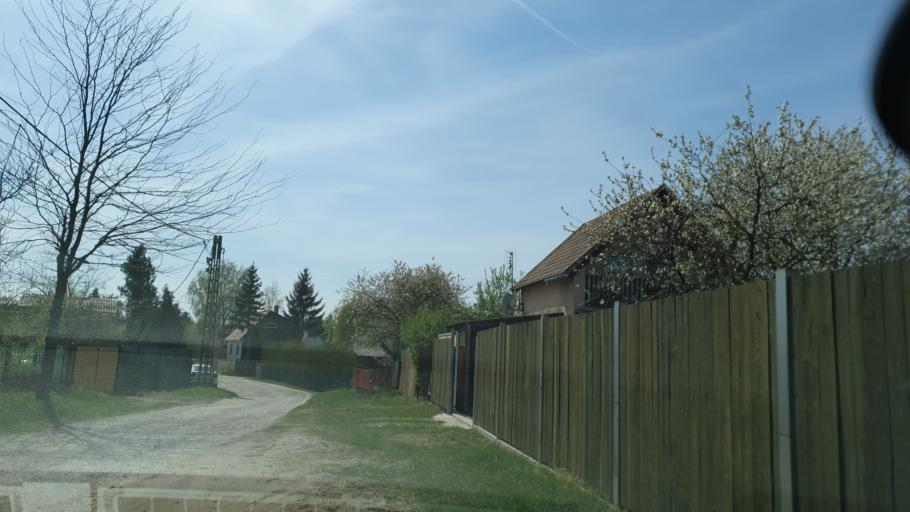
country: HU
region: Komarom-Esztergom
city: Oroszlany
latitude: 47.4967
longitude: 18.2866
